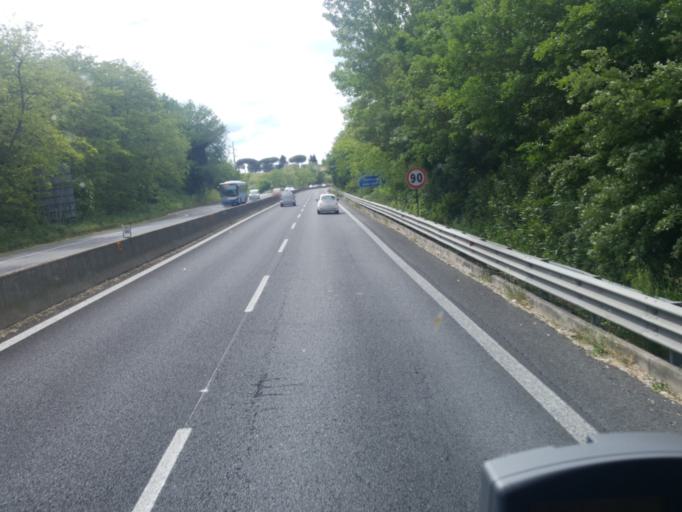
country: IT
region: Latium
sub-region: Citta metropolitana di Roma Capitale
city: Ara Nova
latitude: 41.9104
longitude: 12.2574
